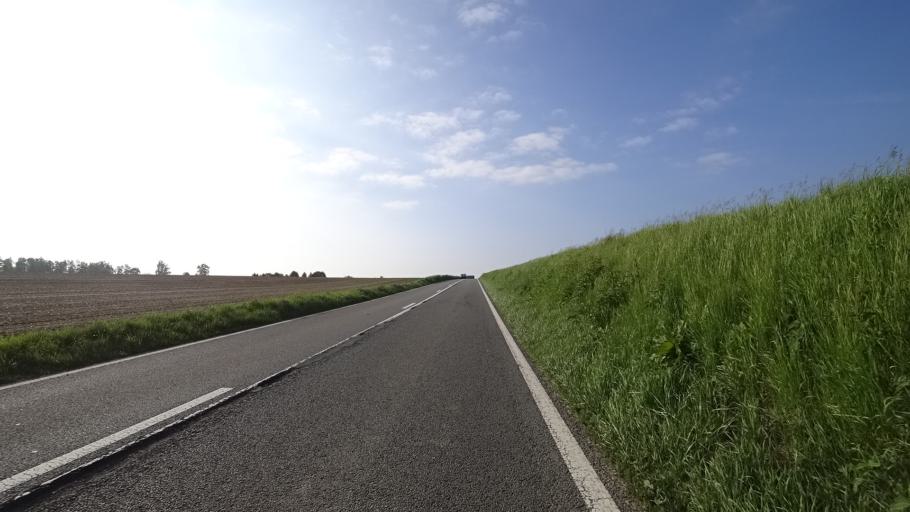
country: BE
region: Wallonia
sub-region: Province de Namur
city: Namur
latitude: 50.4995
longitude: 4.8535
